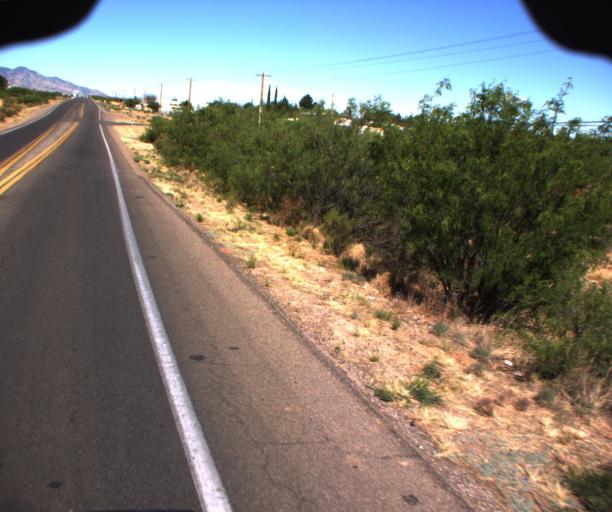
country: US
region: Arizona
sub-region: Cochise County
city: Sierra Vista
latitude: 31.5547
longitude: -110.2169
